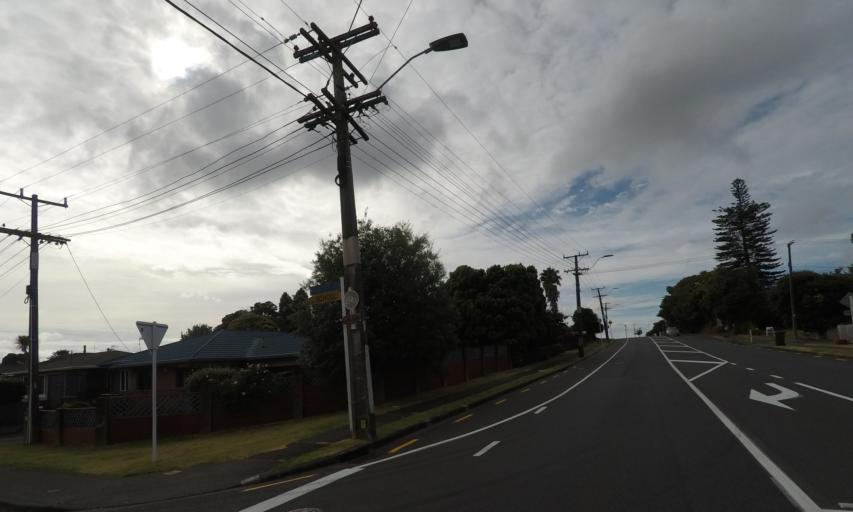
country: NZ
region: Northland
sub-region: Whangarei
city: Whangarei
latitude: -35.6885
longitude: 174.3038
